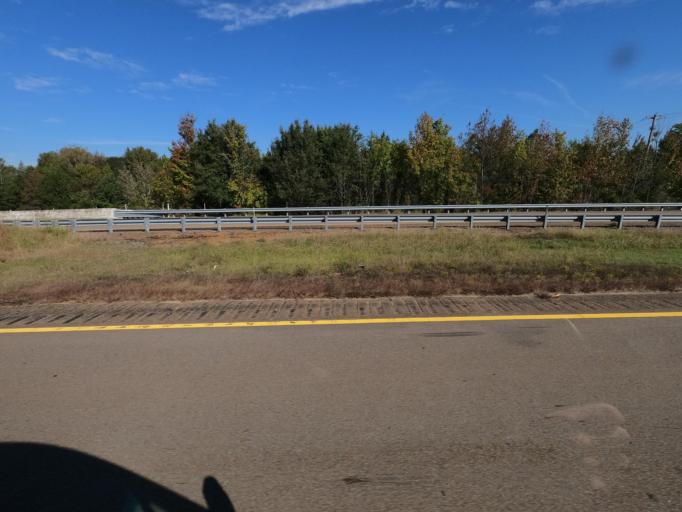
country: US
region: Tennessee
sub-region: Shelby County
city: Lakeland
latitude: 35.3100
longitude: -89.7619
